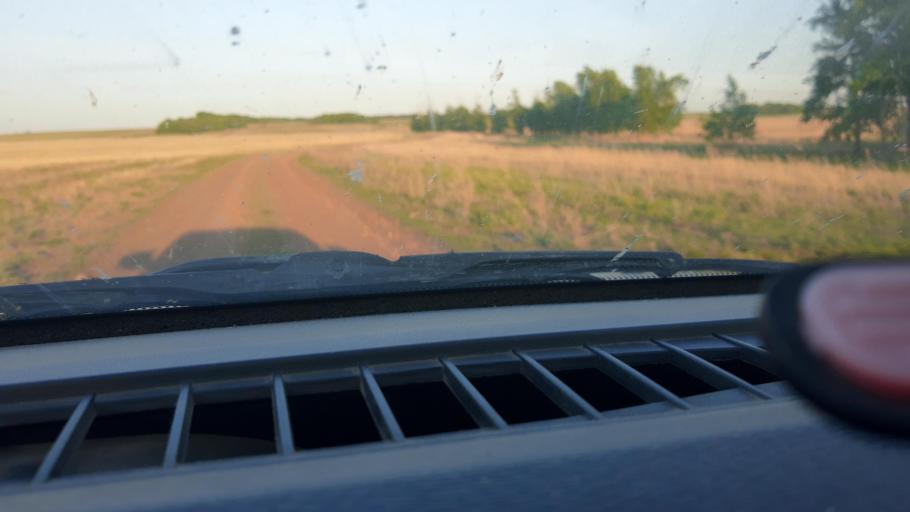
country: RU
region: Bashkortostan
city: Asanovo
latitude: 54.8803
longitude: 55.5036
